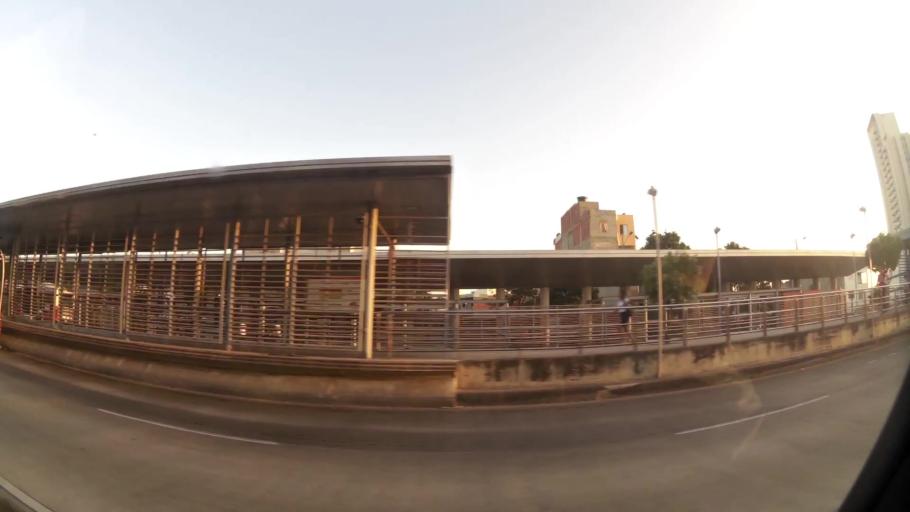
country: CO
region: Bolivar
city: Cartagena
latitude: 10.3953
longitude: -75.4788
